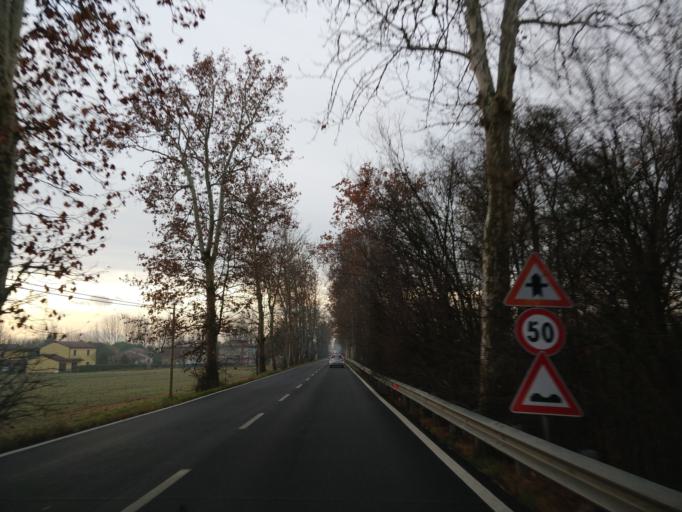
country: IT
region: Emilia-Romagna
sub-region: Provincia di Ferrara
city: Corpo Reno
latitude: 44.7611
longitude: 11.3050
